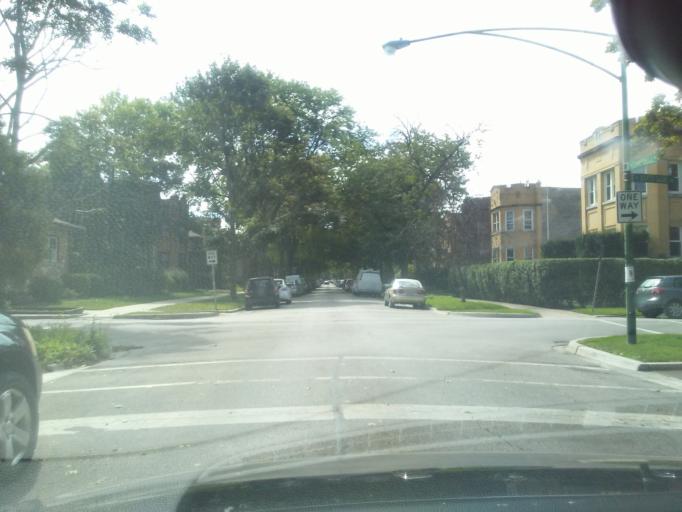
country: US
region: Illinois
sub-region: Cook County
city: Lincolnwood
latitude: 42.0033
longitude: -87.6925
